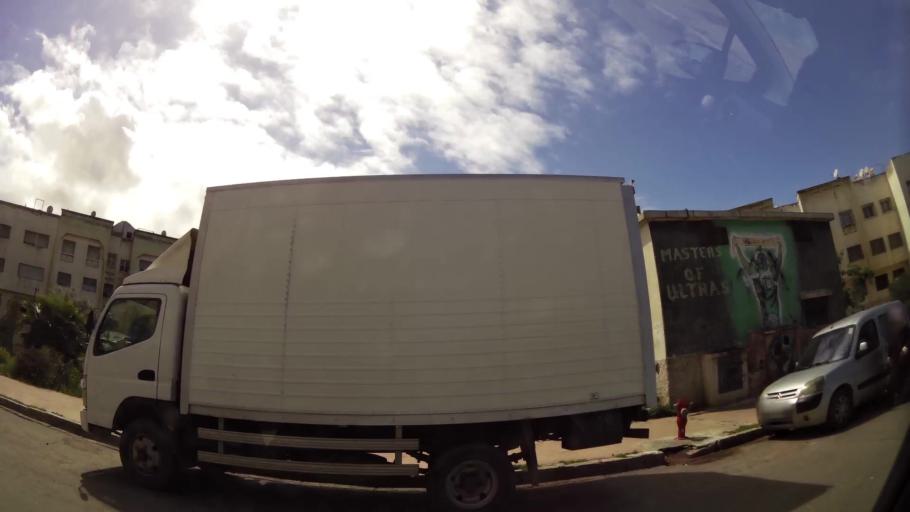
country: MA
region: Grand Casablanca
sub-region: Mediouna
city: Tit Mellil
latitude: 33.6032
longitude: -7.4815
